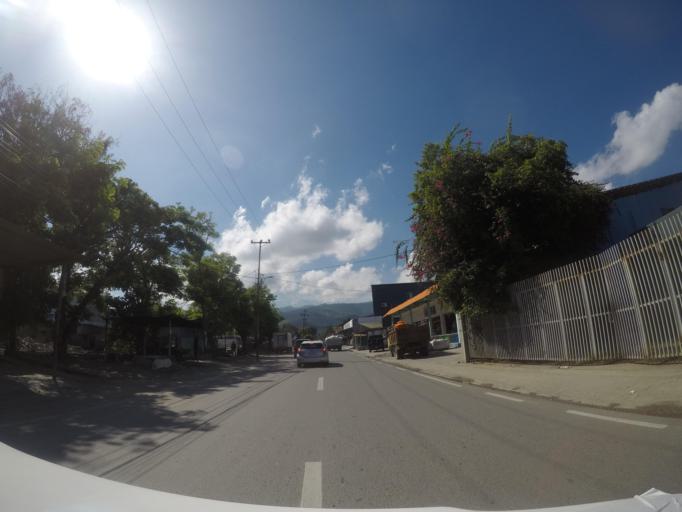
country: TL
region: Dili
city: Dili
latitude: -8.5500
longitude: 125.5898
